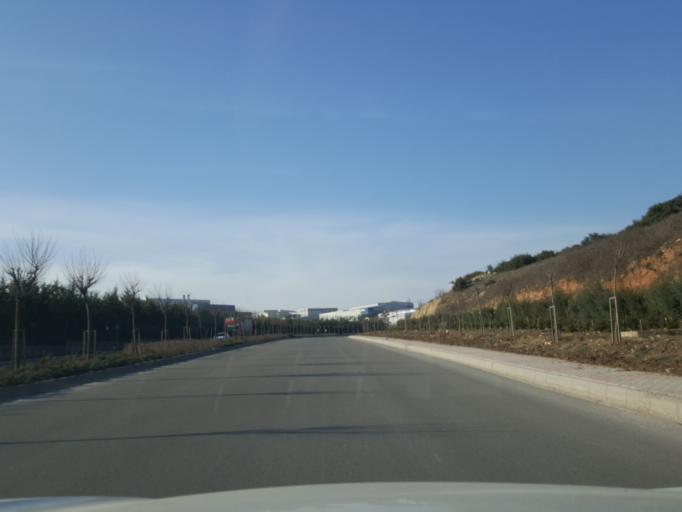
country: TR
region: Kocaeli
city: Tavsancil
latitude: 40.8140
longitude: 29.5668
